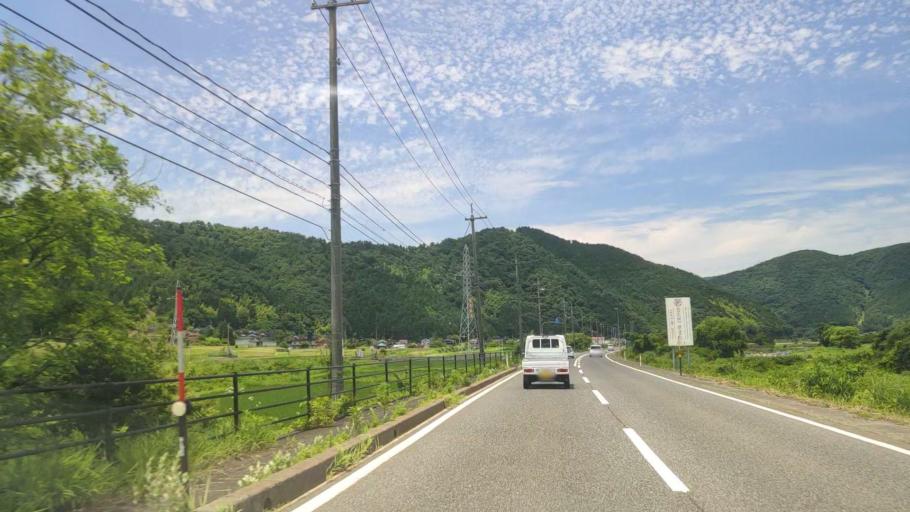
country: JP
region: Tottori
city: Tottori
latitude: 35.3532
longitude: 134.3851
